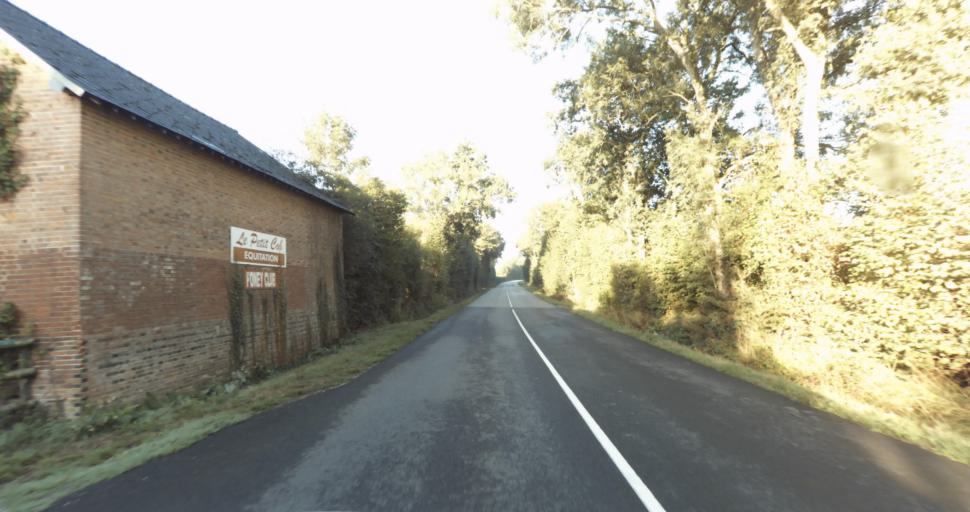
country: FR
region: Lower Normandy
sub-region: Departement de l'Orne
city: Vimoutiers
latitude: 48.8983
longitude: 0.1310
